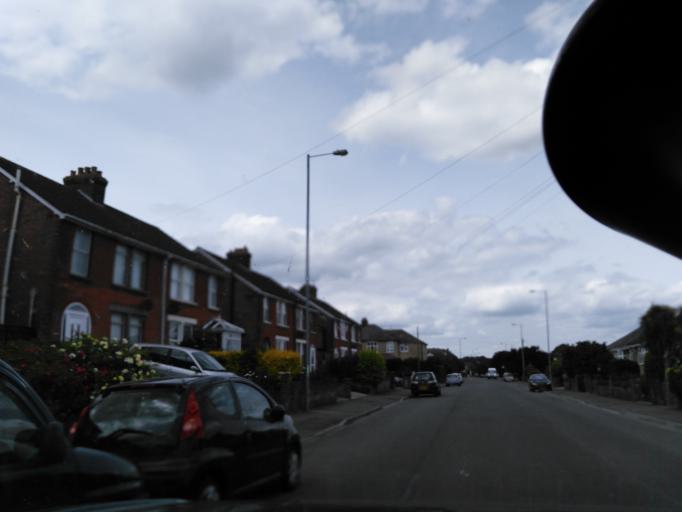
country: GB
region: England
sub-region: Wiltshire
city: Salisbury
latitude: 51.0840
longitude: -1.8209
